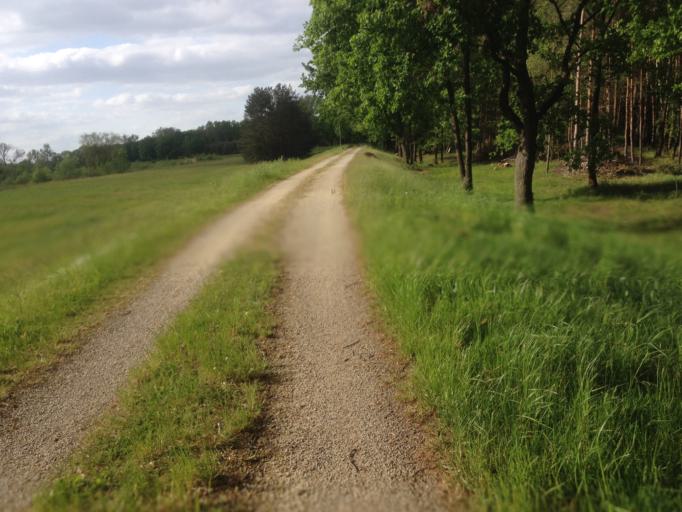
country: DE
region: Brandenburg
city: Drehnow
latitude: 51.8327
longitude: 14.3488
